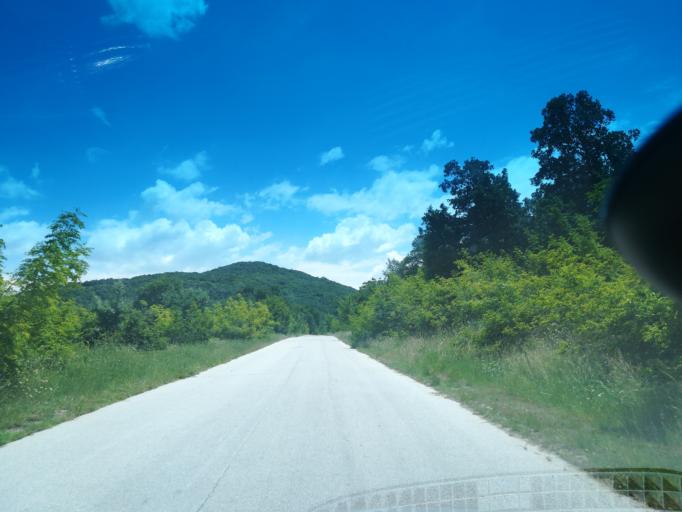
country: BG
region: Khaskovo
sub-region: Obshtina Mineralni Bani
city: Mineralni Bani
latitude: 41.9744
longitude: 25.2581
